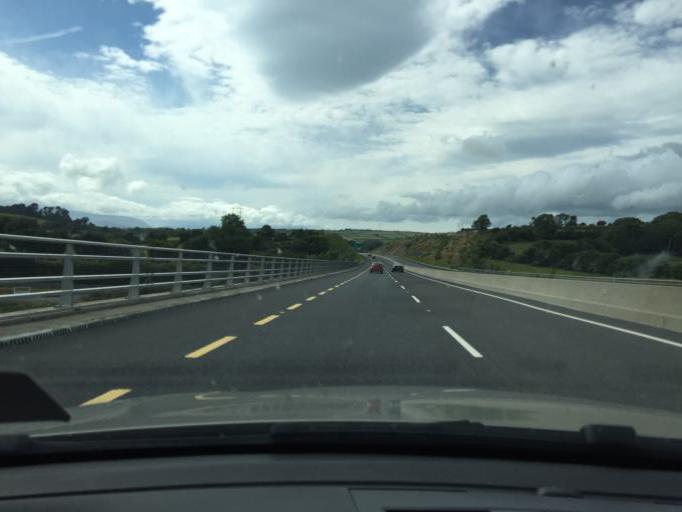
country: IE
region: Leinster
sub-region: Kilkenny
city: Mooncoin
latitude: 52.2384
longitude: -7.2381
